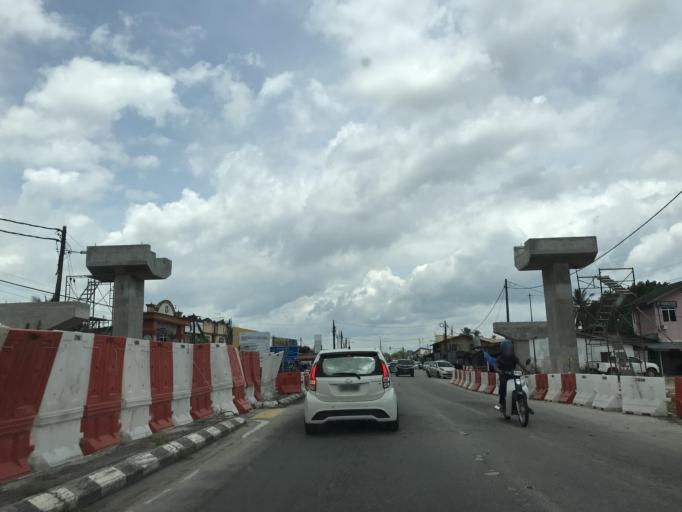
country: MY
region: Kelantan
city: Pasir Mas
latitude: 6.0687
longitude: 102.2066
